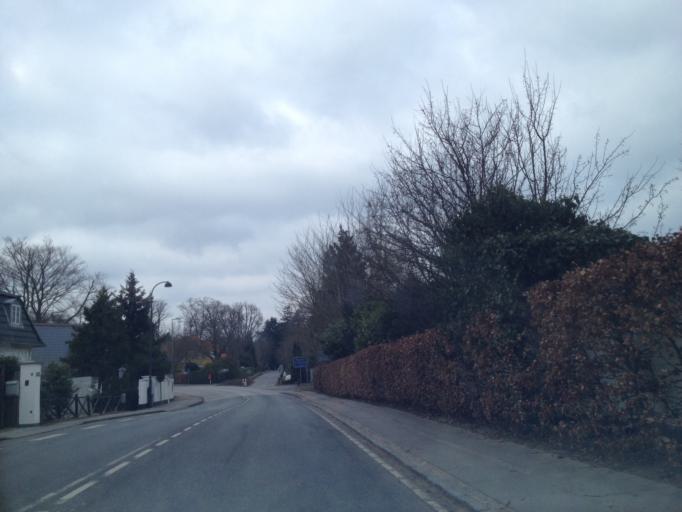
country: DK
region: Capital Region
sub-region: Rudersdal Kommune
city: Trorod
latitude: 55.8619
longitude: 12.5595
